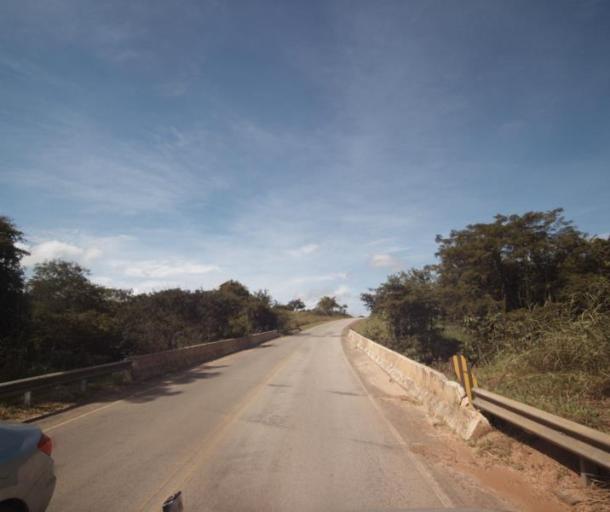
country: BR
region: Goias
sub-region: Abadiania
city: Abadiania
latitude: -16.1376
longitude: -48.8916
